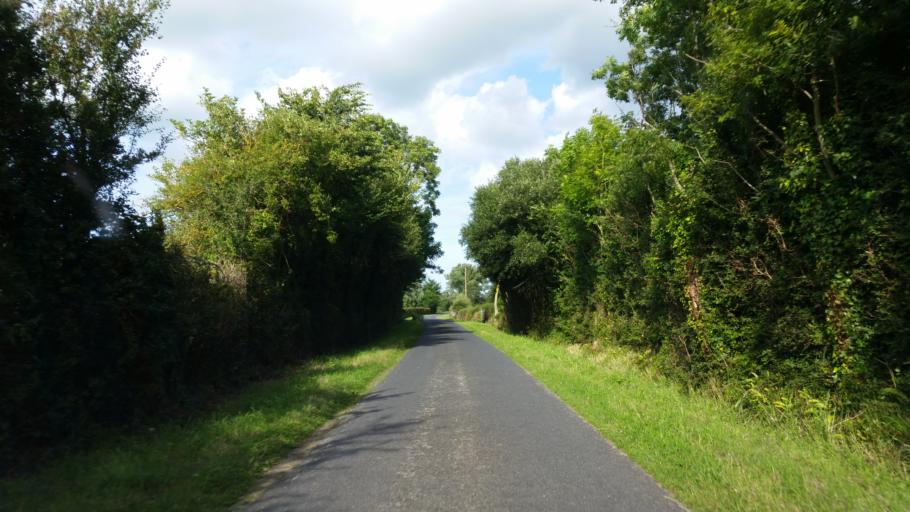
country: FR
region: Lower Normandy
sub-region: Departement de la Manche
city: Sainte-Mere-Eglise
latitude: 49.4503
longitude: -1.2521
